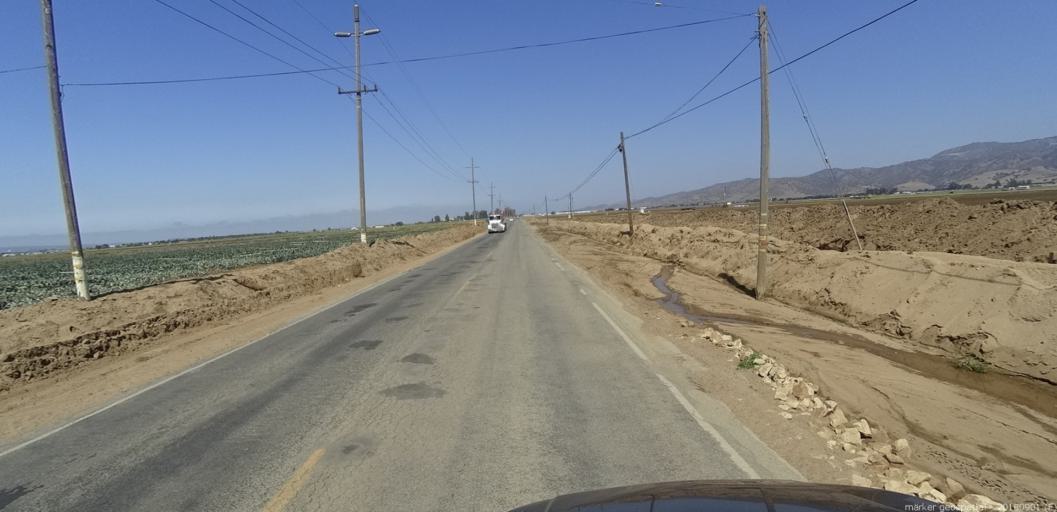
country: US
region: California
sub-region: Monterey County
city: Chualar
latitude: 36.6001
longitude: -121.5098
